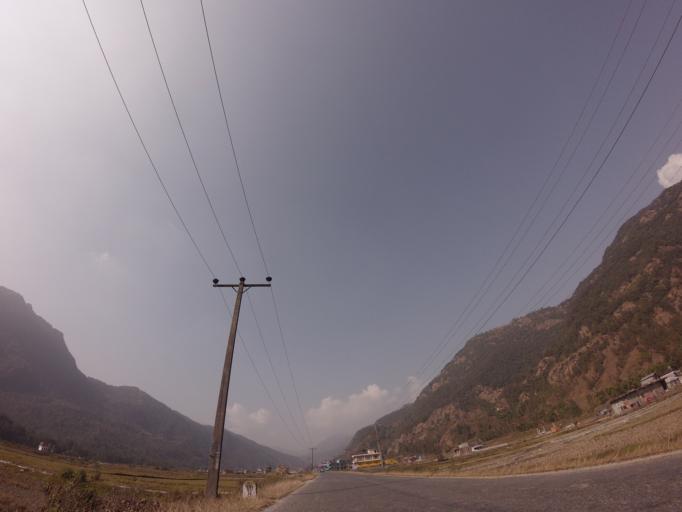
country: NP
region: Western Region
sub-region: Gandaki Zone
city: Pokhara
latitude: 28.2842
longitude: 83.9178
